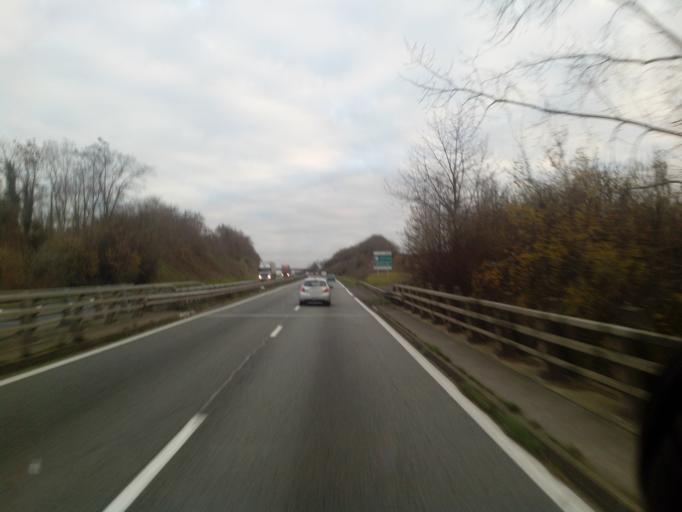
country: FR
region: Poitou-Charentes
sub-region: Departement de la Vienne
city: Migne-Auxances
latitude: 46.6250
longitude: 0.2992
